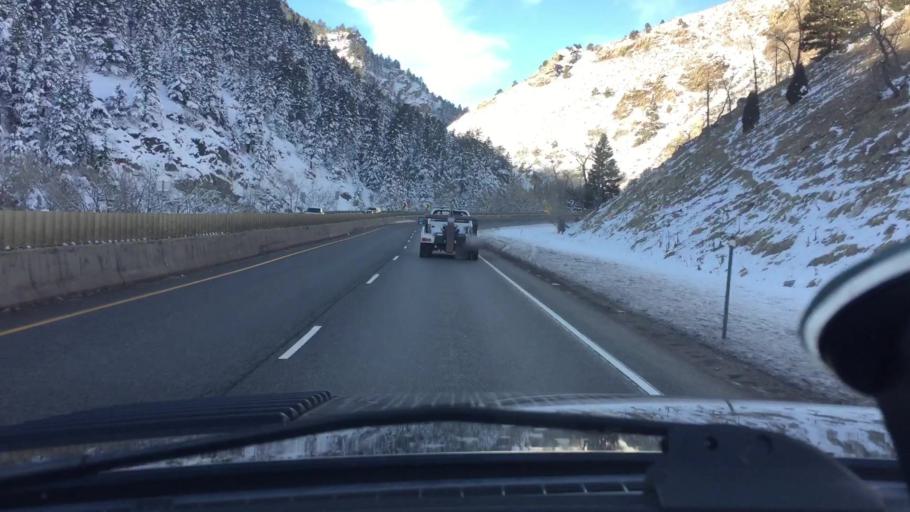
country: US
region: Colorado
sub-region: Jefferson County
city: Indian Hills
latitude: 39.6190
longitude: -105.2086
